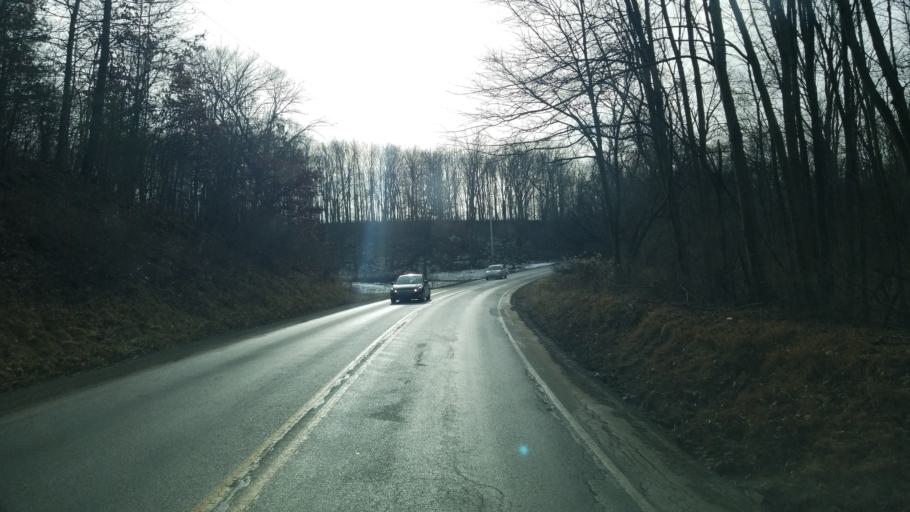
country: US
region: Pennsylvania
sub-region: Jefferson County
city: Punxsutawney
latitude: 40.8881
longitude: -79.0410
